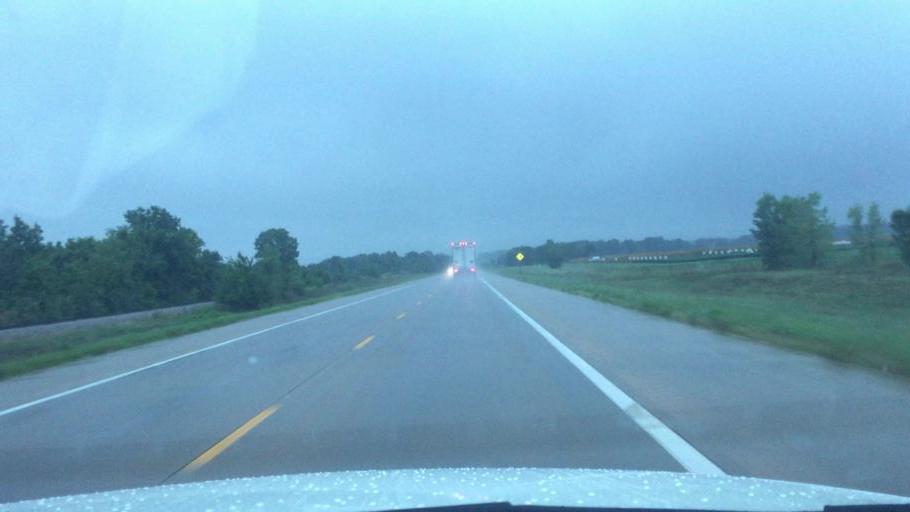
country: US
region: Kansas
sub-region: Neosho County
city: Chanute
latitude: 37.5651
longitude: -95.4710
